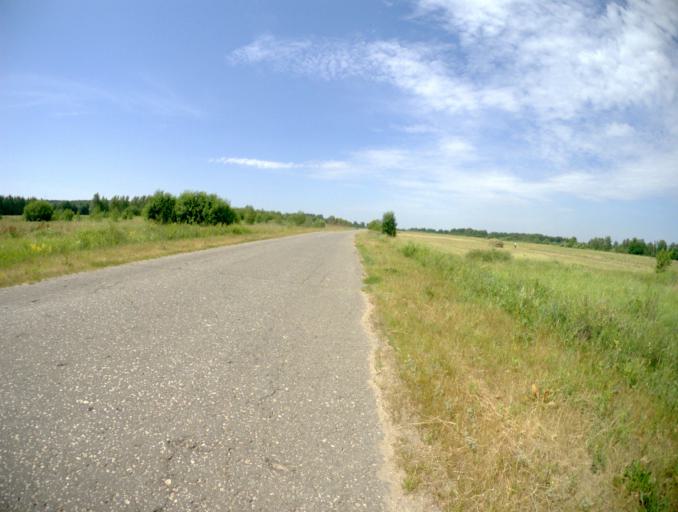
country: RU
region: Vladimir
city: Vorsha
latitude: 56.0226
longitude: 40.2044
